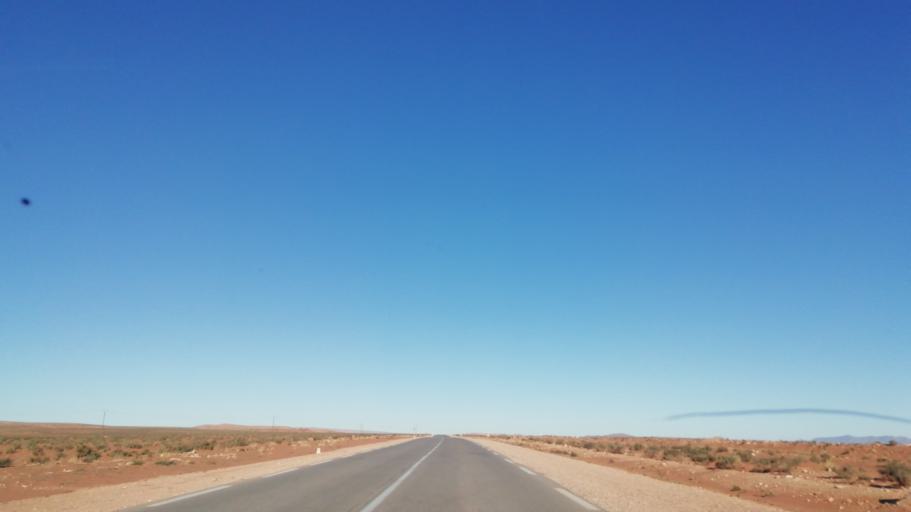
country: DZ
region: El Bayadh
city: El Abiodh Sidi Cheikh
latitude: 33.1246
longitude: 0.2800
